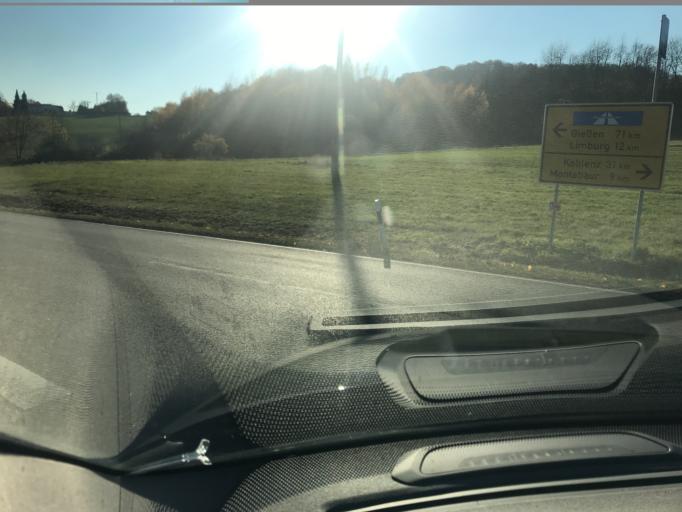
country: DE
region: Rheinland-Pfalz
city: Eppenrod
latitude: 50.4261
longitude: 7.9293
